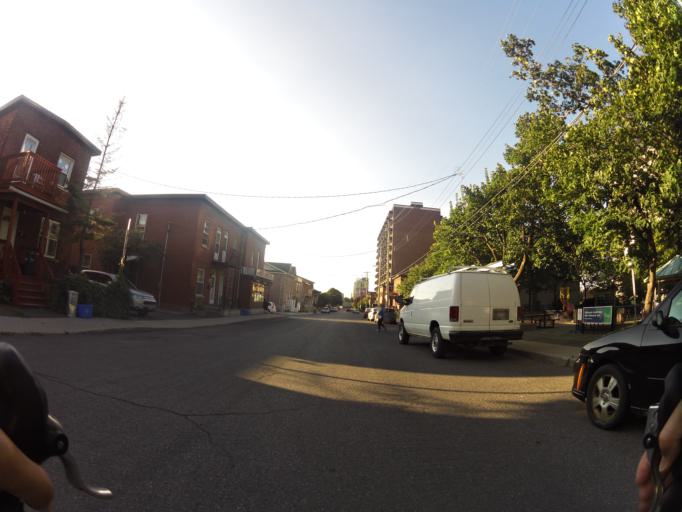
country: CA
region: Ontario
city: Ottawa
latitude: 45.4019
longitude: -75.7030
